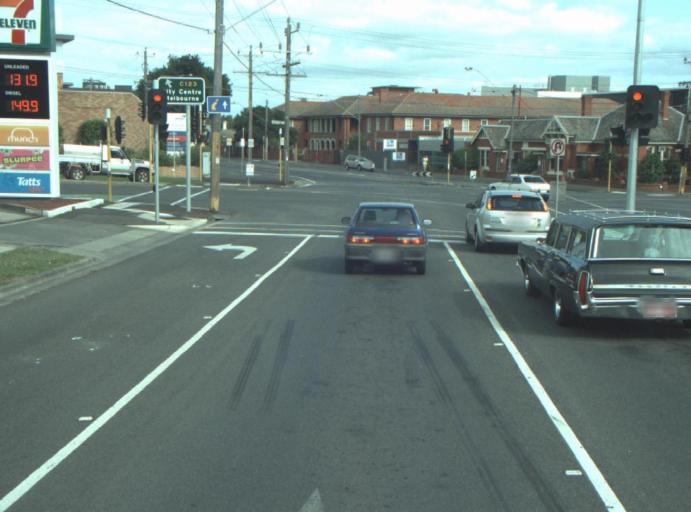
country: AU
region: Victoria
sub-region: Greater Geelong
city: East Geelong
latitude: -38.1519
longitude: 144.3677
